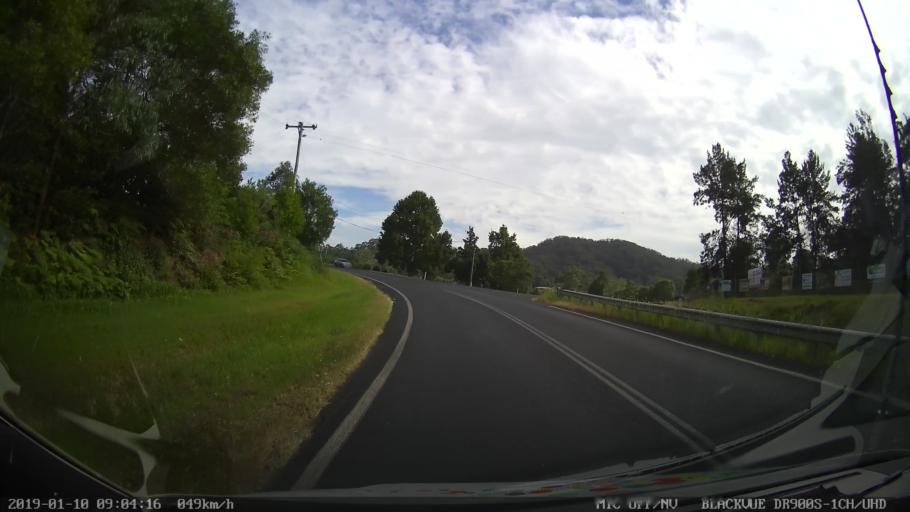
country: AU
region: New South Wales
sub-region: Coffs Harbour
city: Coffs Harbour
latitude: -30.2576
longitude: 153.0525
